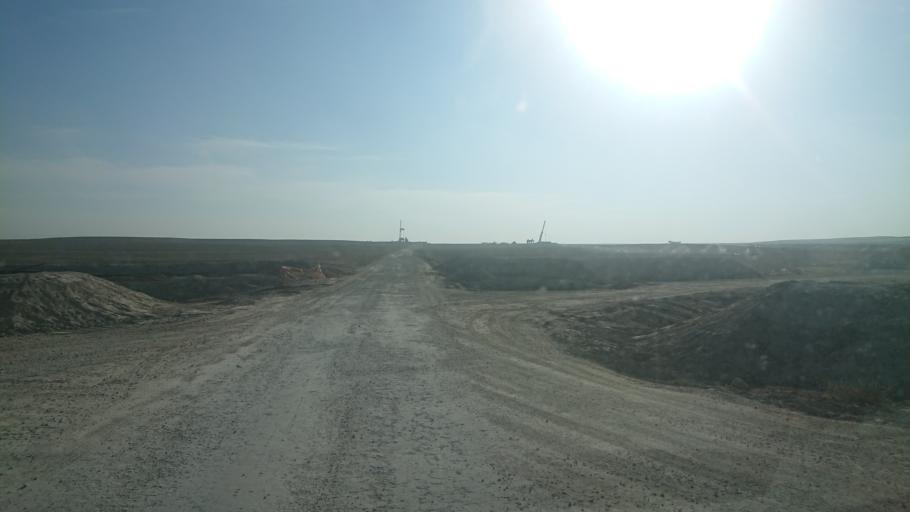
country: TR
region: Aksaray
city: Sultanhani
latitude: 38.0682
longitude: 33.6161
